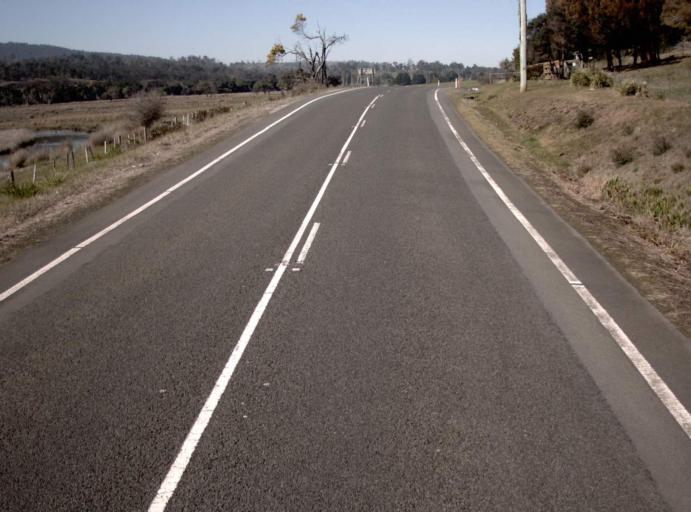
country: AU
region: Tasmania
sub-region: Launceston
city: Mayfield
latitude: -41.3183
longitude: 147.0574
